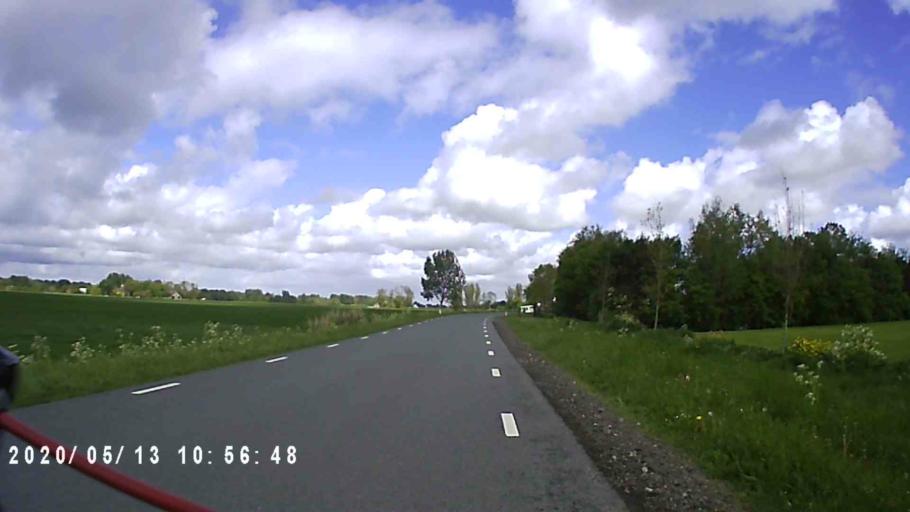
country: NL
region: Groningen
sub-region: Gemeente Zuidhorn
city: Grijpskerk
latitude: 53.2711
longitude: 6.3350
